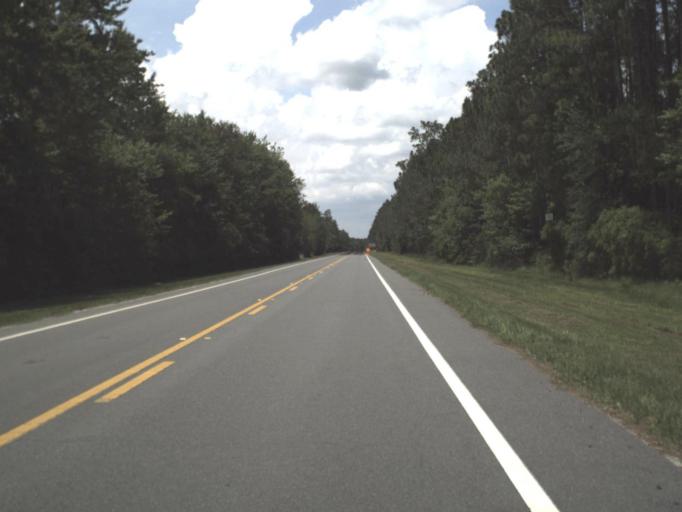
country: US
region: Georgia
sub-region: Camden County
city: Kingsland
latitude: 30.7218
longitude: -81.6795
